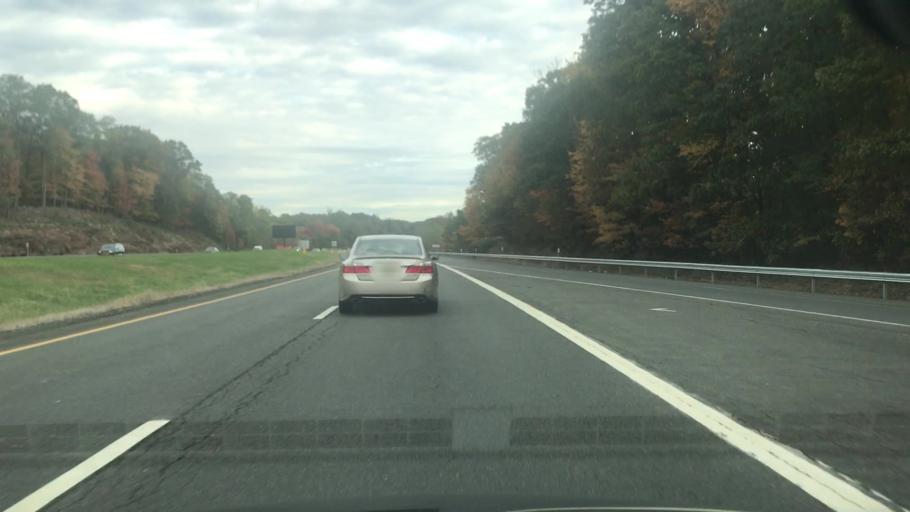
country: US
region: New York
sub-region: Rockland County
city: Chestnut Ridge
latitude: 41.0720
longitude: -74.0524
